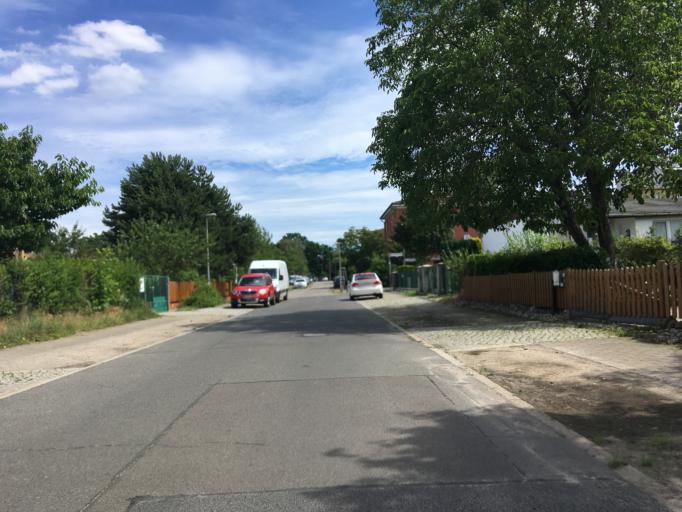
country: DE
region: Berlin
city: Altglienicke
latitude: 52.4209
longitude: 13.5298
